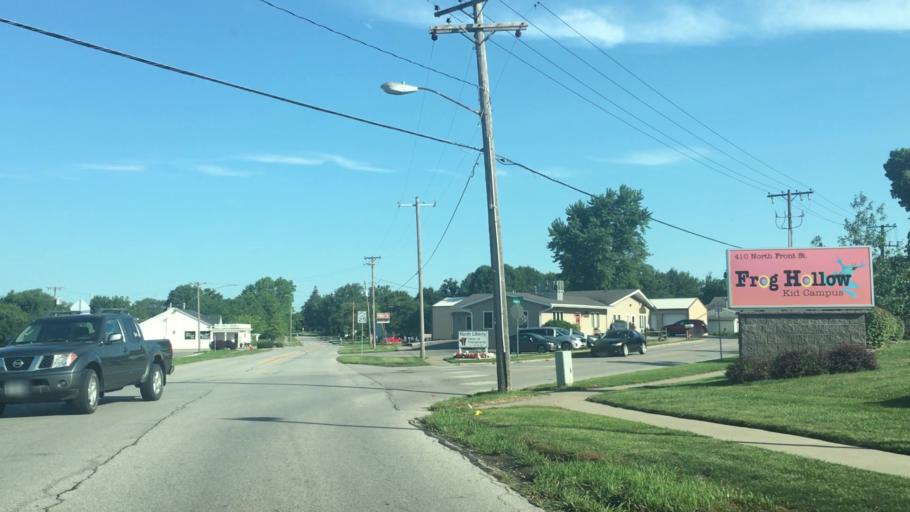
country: US
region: Iowa
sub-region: Johnson County
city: North Liberty
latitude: 41.7491
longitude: -91.5978
